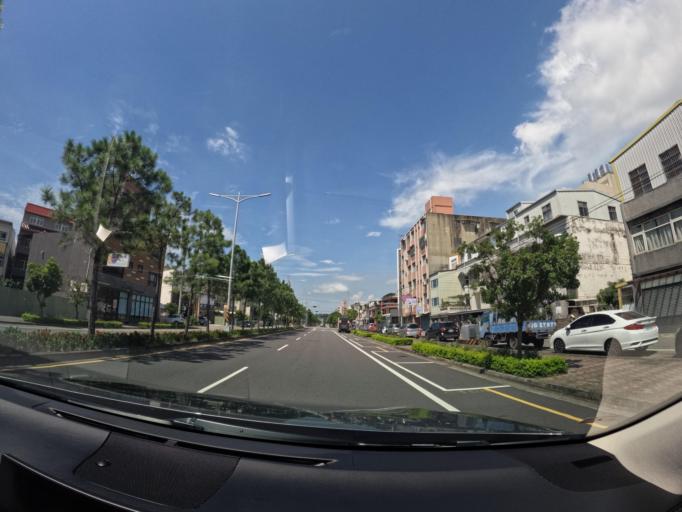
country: TW
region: Taiwan
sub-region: Hsinchu
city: Hsinchu
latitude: 24.6942
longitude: 120.9068
